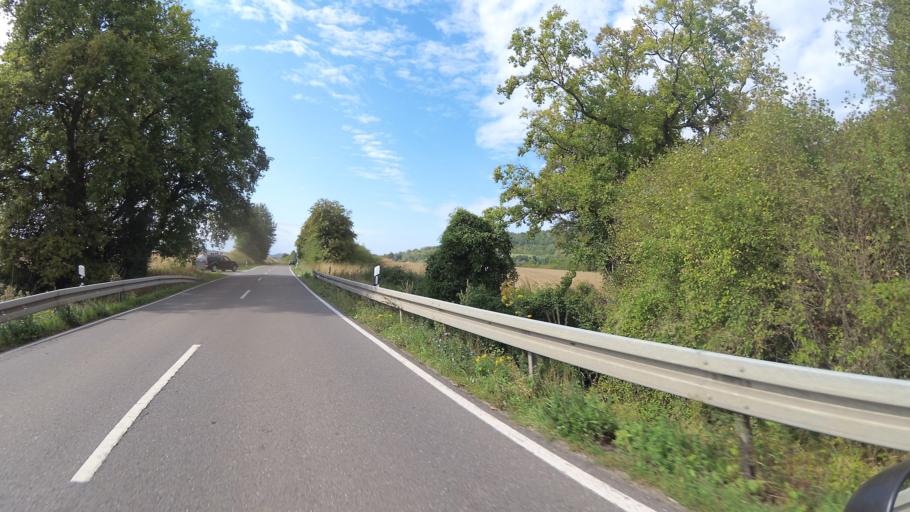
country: DE
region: Saarland
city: Gersheim
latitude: 49.1597
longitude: 7.2151
